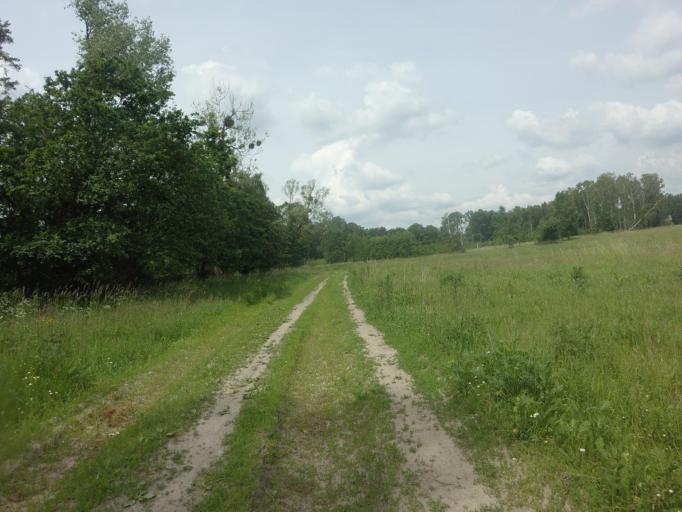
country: PL
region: West Pomeranian Voivodeship
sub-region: Powiat stargardzki
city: Dobrzany
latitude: 53.3013
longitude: 15.4717
